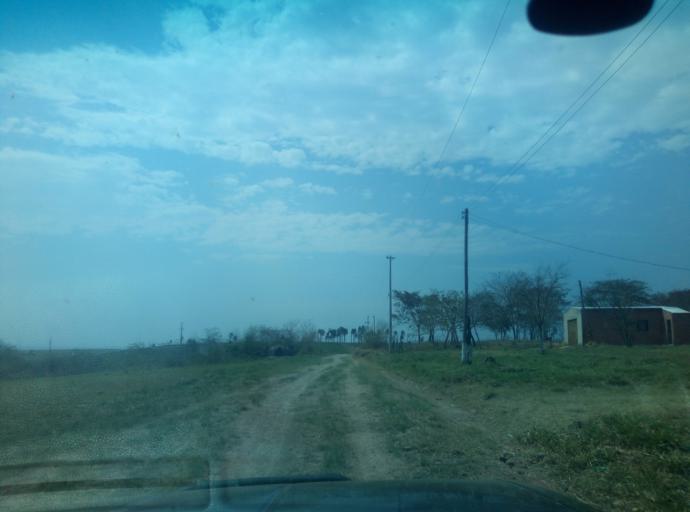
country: PY
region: Caaguazu
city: Doctor Cecilio Baez
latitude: -25.1379
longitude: -56.1593
